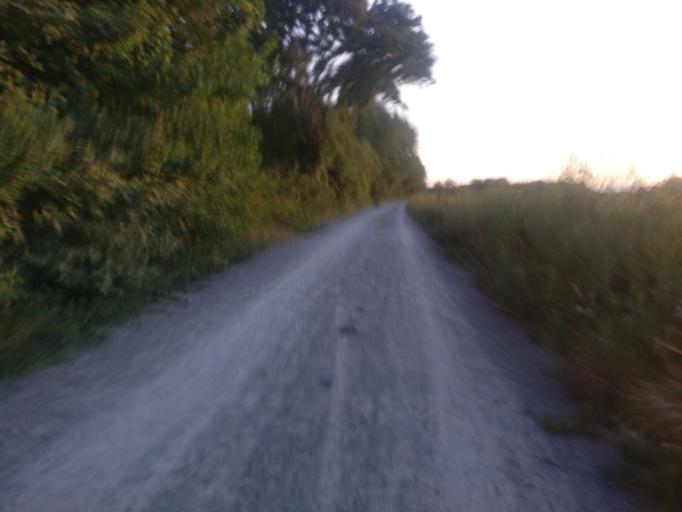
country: AT
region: Lower Austria
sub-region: Politischer Bezirk Baden
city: Ebreichsdorf
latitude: 47.9593
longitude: 16.4245
